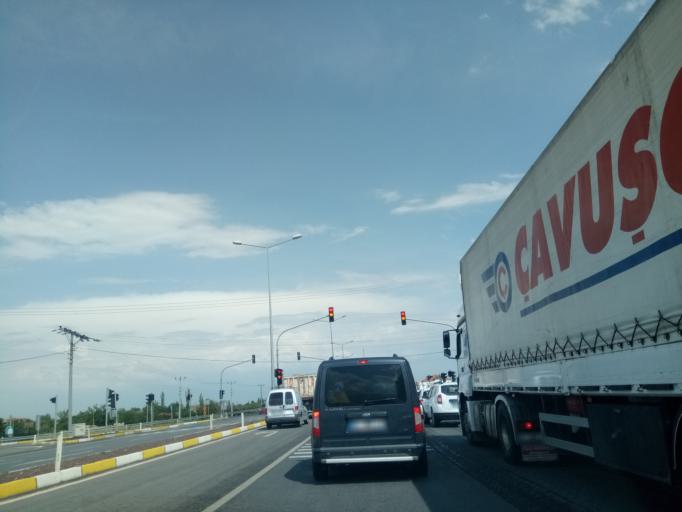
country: TR
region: Konya
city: Aksehir
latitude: 38.3789
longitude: 31.4222
